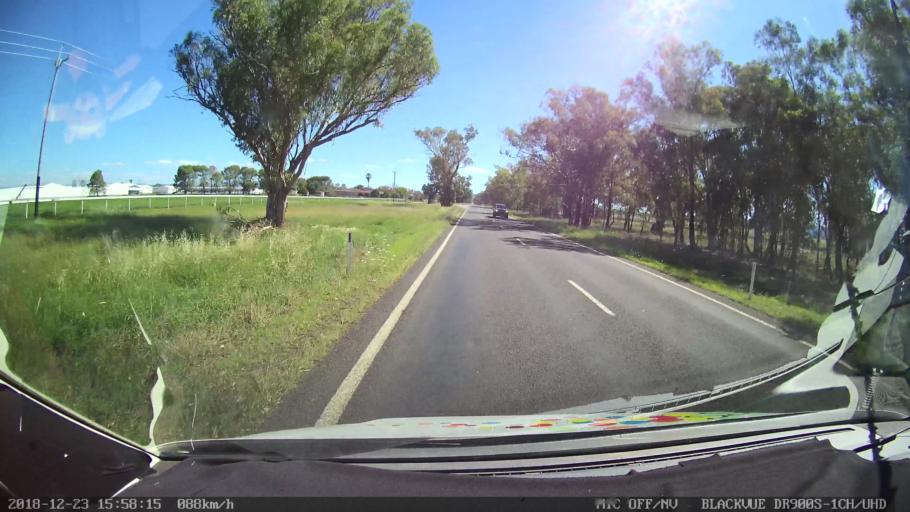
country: AU
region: New South Wales
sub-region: Tamworth Municipality
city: Phillip
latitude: -31.1862
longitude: 150.8432
